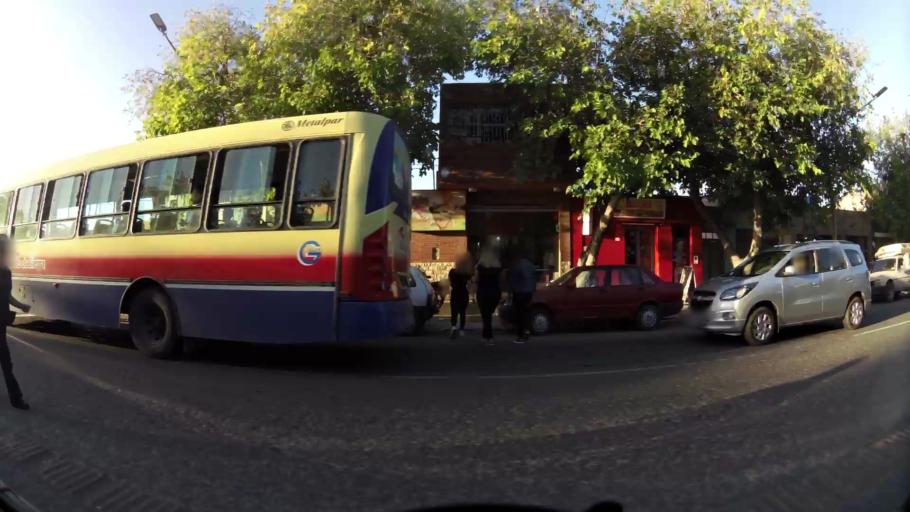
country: AR
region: San Juan
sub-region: Departamento de Santa Lucia
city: Santa Lucia
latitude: -31.5414
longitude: -68.4954
